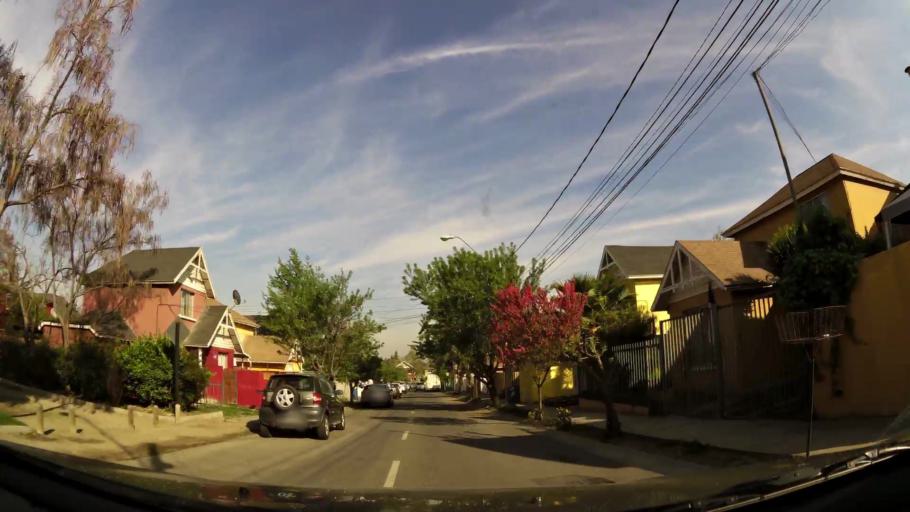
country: CL
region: Santiago Metropolitan
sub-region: Provincia de Cordillera
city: Puente Alto
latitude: -33.5582
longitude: -70.5462
